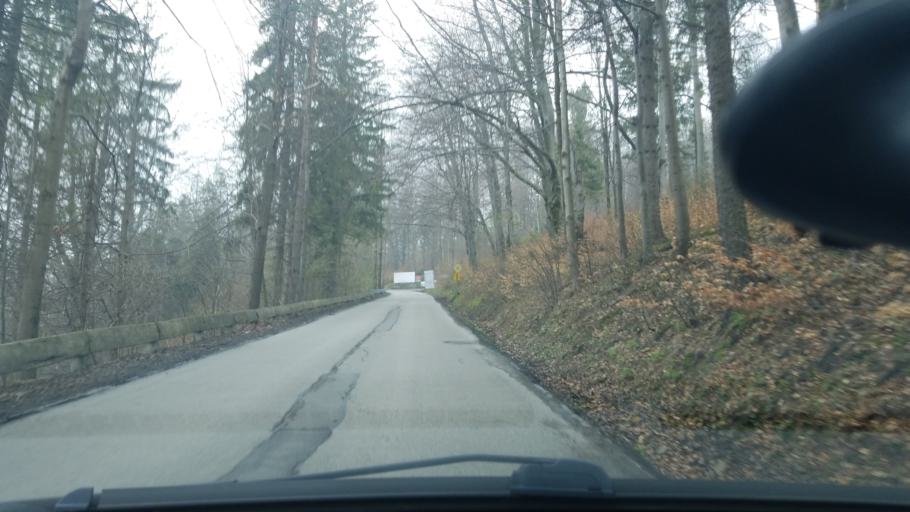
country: PL
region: Silesian Voivodeship
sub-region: Powiat cieszynski
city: Ustron
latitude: 49.7156
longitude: 18.8468
